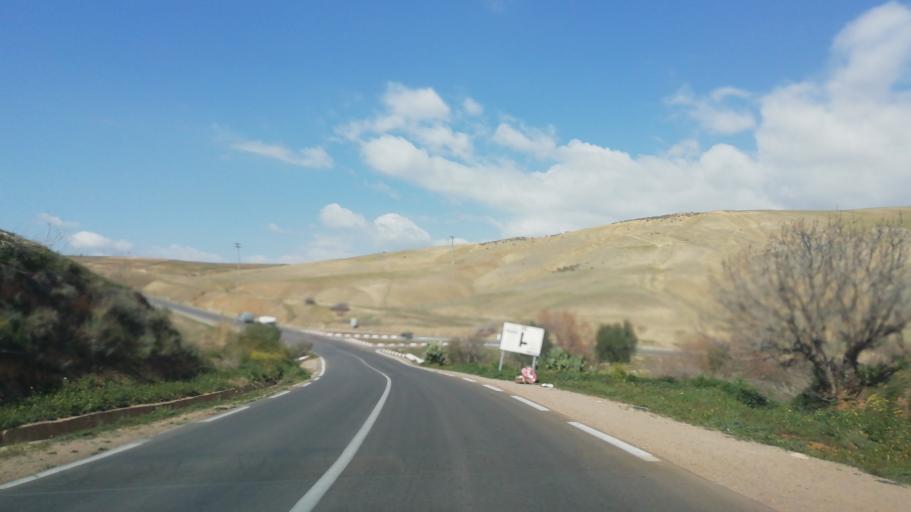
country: DZ
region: Mascara
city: Mascara
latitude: 35.5388
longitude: 0.1137
